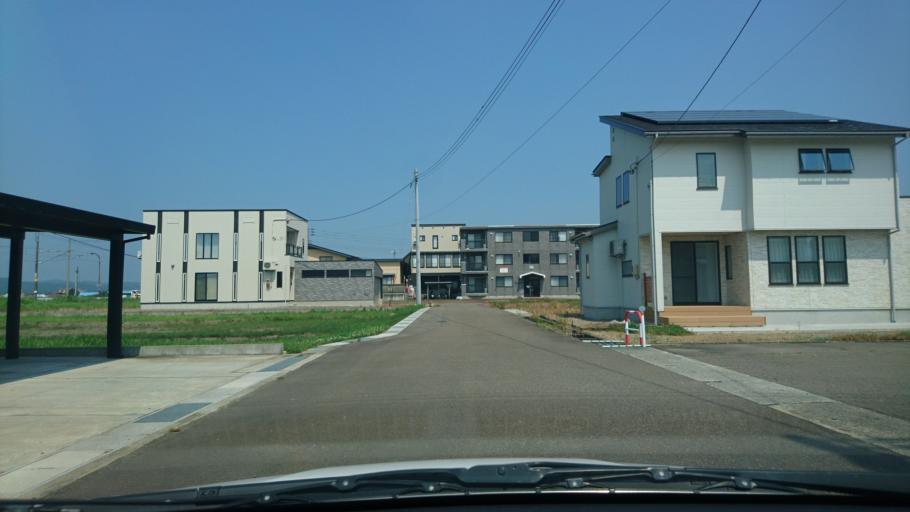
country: JP
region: Niigata
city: Arai
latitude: 37.0527
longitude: 138.2582
